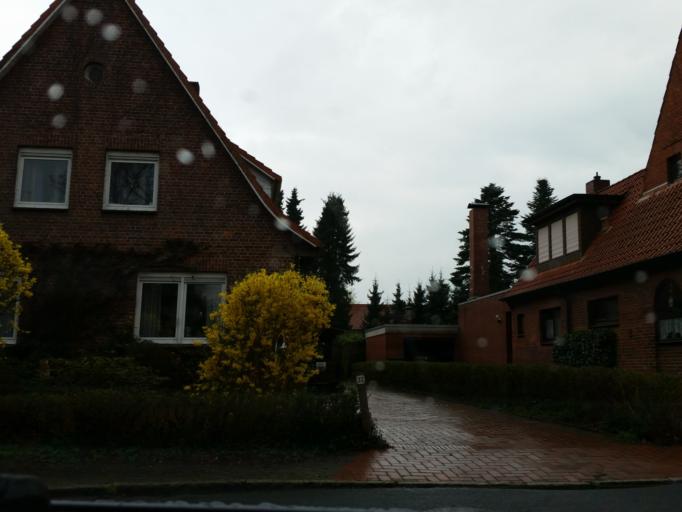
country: DE
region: Lower Saxony
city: Bremervorde
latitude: 53.4858
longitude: 9.1396
